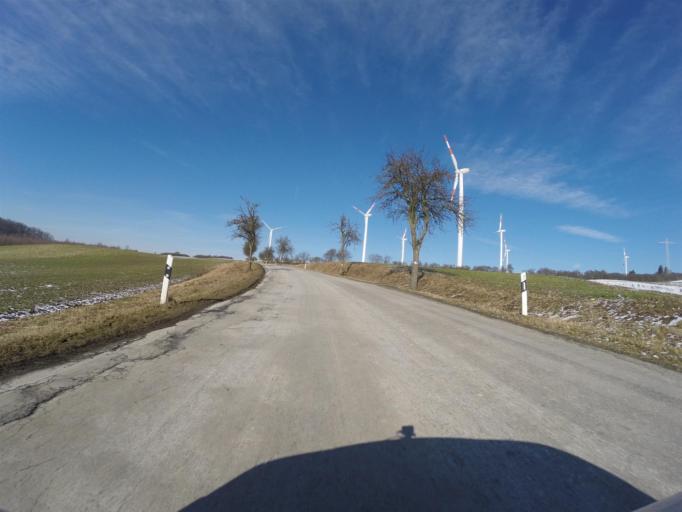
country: DE
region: Thuringia
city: Bucha
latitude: 50.8934
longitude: 11.5089
